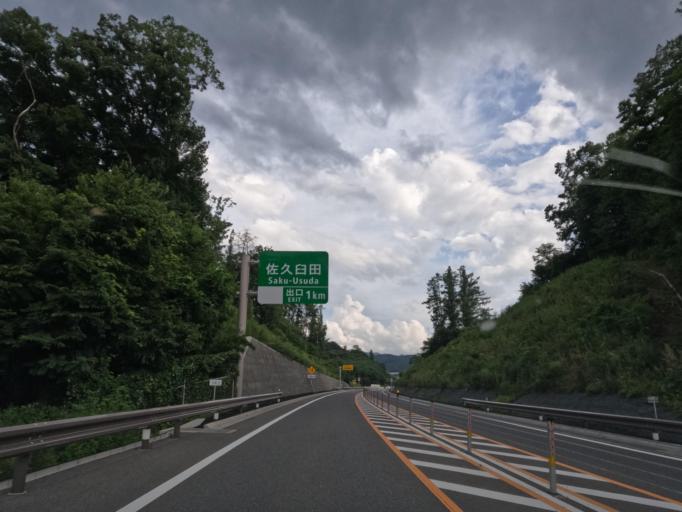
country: JP
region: Nagano
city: Saku
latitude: 36.1942
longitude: 138.4681
